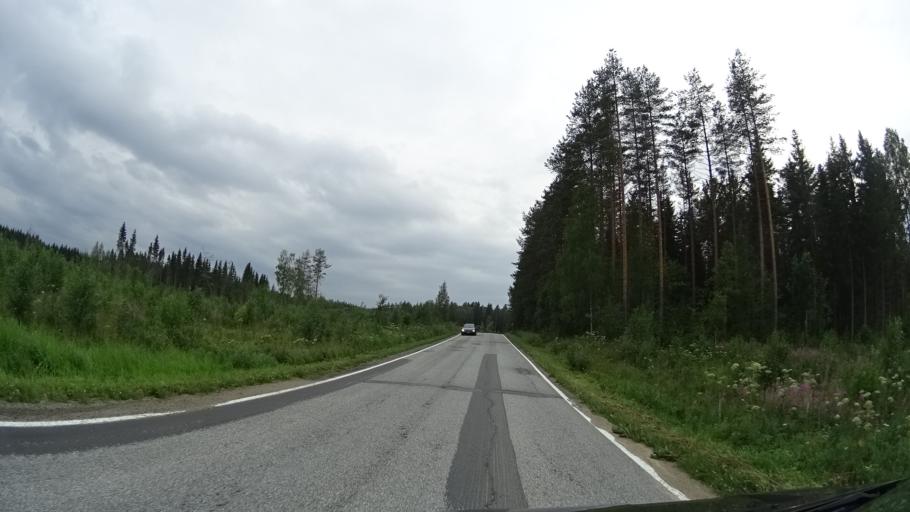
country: FI
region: Southern Savonia
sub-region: Savonlinna
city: Punkaharju
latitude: 61.7488
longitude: 29.5059
